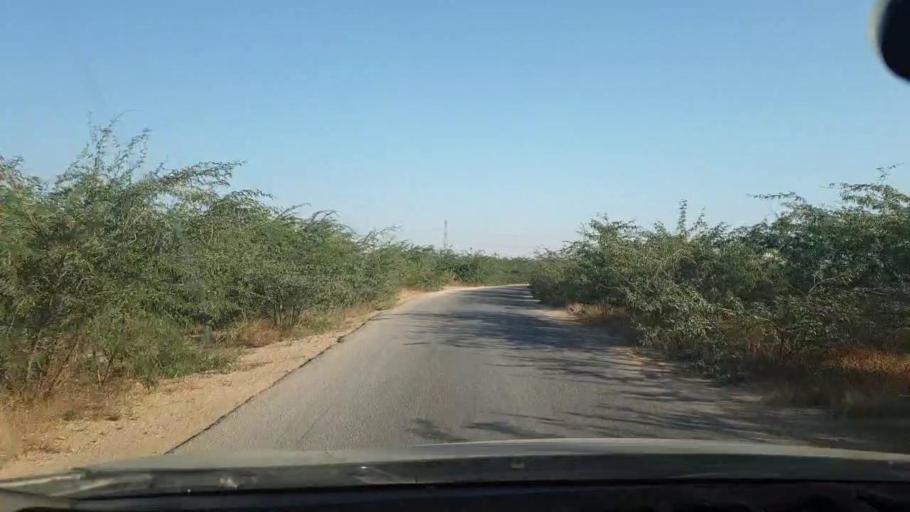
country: PK
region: Sindh
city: Malir Cantonment
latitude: 25.1553
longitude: 67.1913
